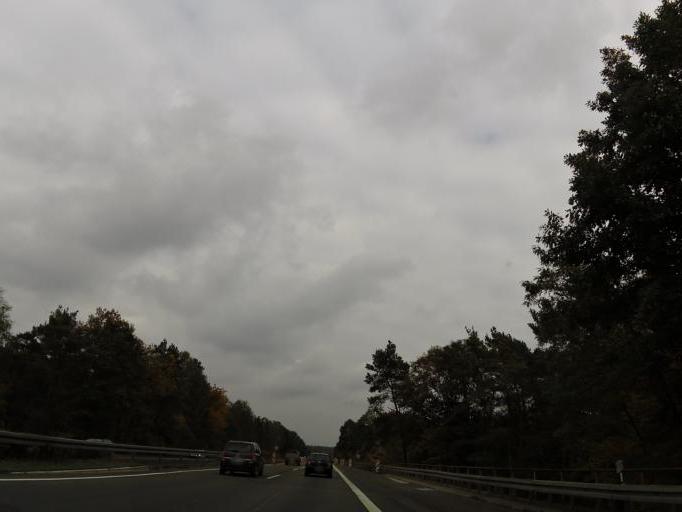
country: DE
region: Rheinland-Pfalz
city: Waldmohr
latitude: 49.3615
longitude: 7.3393
